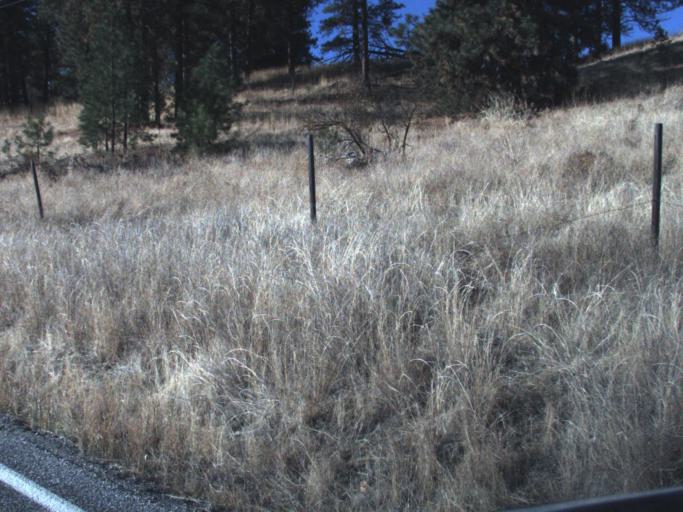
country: CA
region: British Columbia
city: Grand Forks
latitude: 48.8914
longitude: -118.5978
